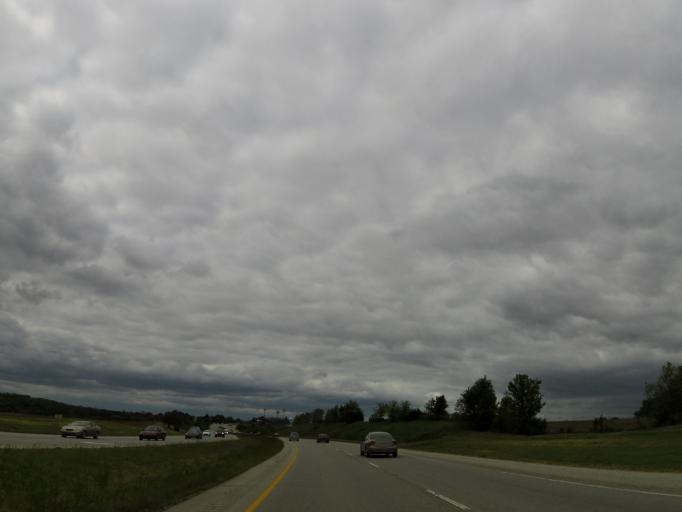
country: US
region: Kentucky
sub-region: Scott County
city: Georgetown
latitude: 38.2051
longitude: -84.5371
